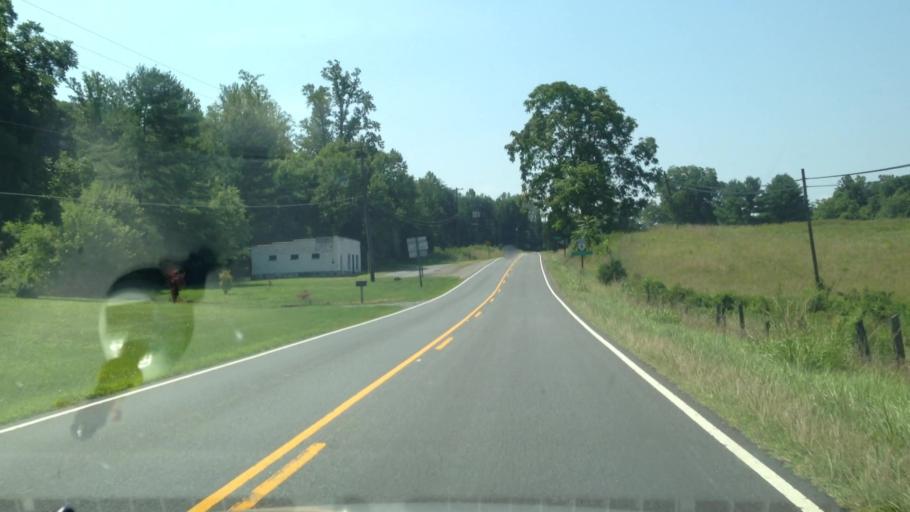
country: US
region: Virginia
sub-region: Patrick County
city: Stuart
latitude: 36.5877
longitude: -80.2799
